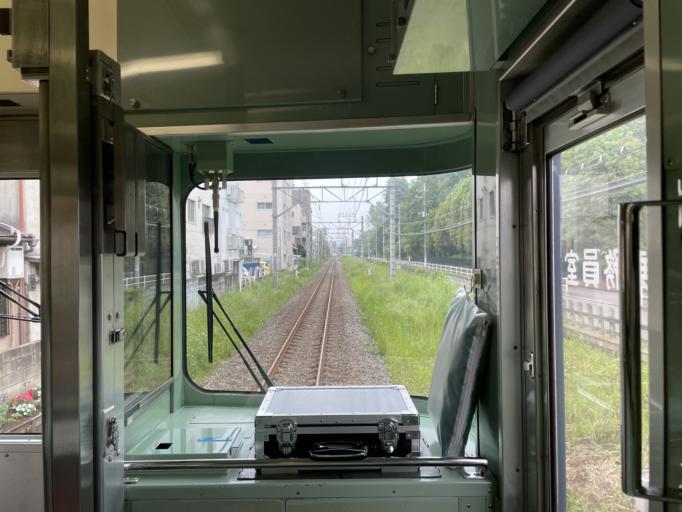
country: JP
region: Tokyo
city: Kokubunji
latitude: 35.7176
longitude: 139.4803
